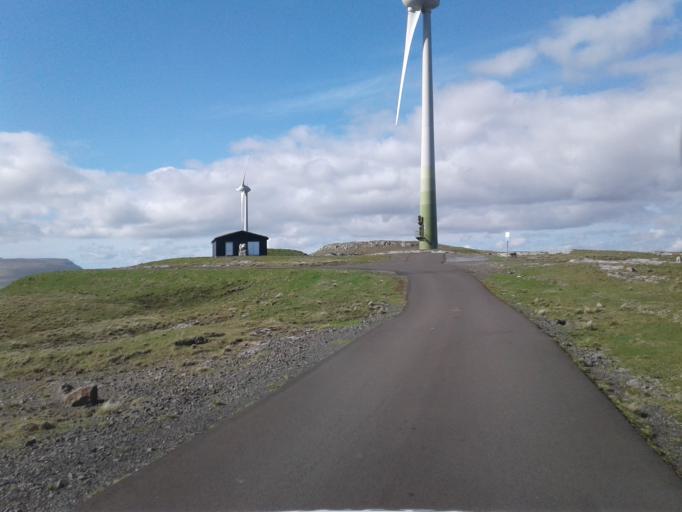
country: FO
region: Streymoy
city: Hoyvik
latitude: 62.0677
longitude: -6.7093
